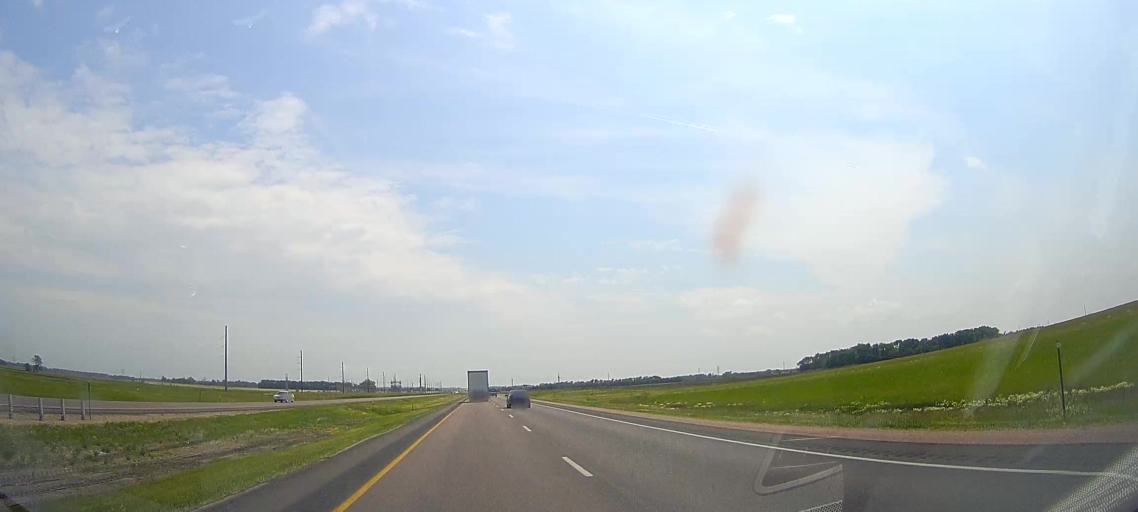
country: US
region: South Dakota
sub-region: Union County
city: Beresford
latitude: 43.1259
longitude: -96.7968
